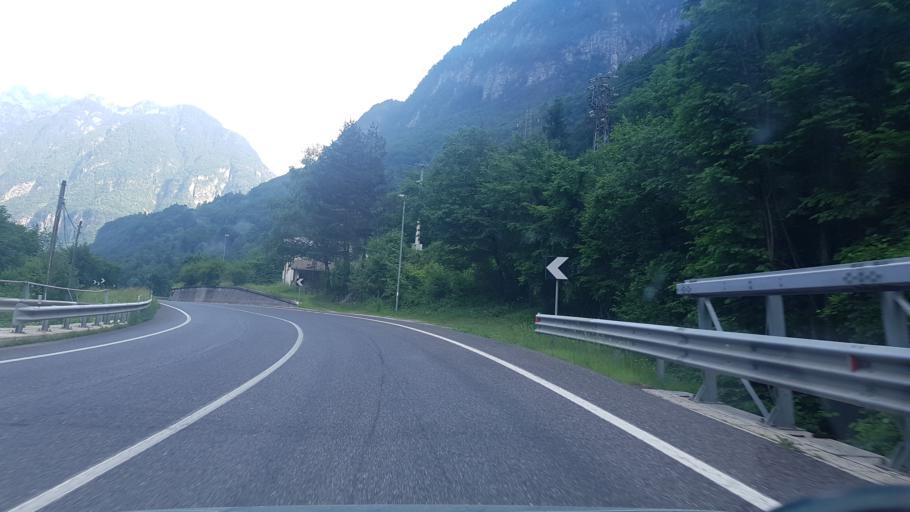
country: IT
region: Friuli Venezia Giulia
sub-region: Provincia di Udine
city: Dogna
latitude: 46.4620
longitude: 13.2951
